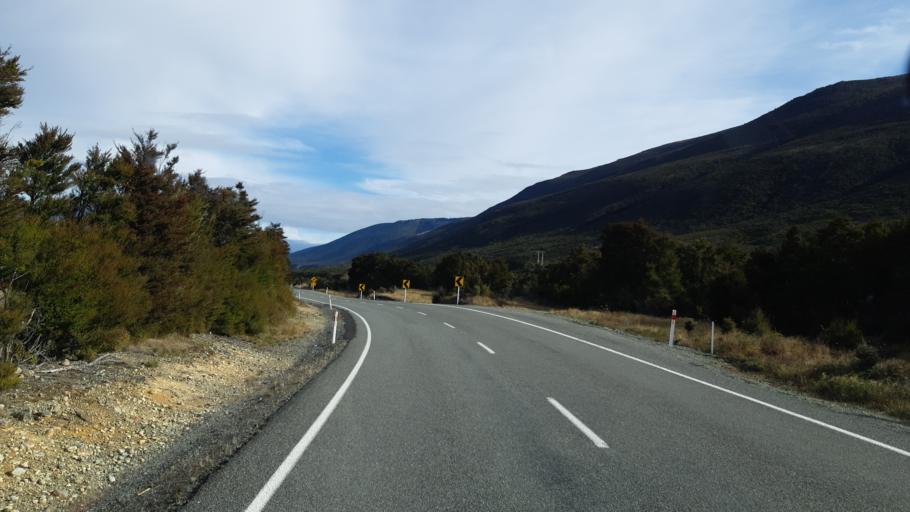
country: NZ
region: Tasman
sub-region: Tasman District
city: Wakefield
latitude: -41.7284
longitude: 173.0404
